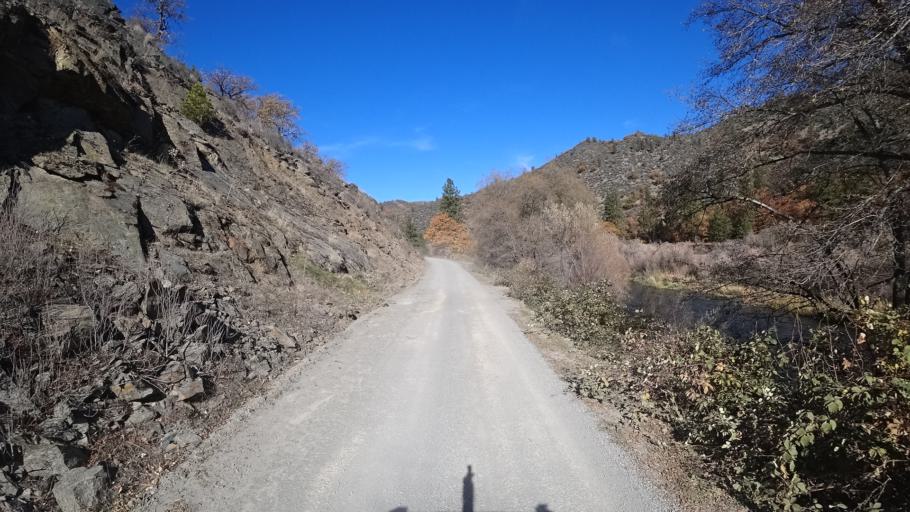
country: US
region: California
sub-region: Siskiyou County
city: Yreka
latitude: 41.8446
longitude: -122.6846
